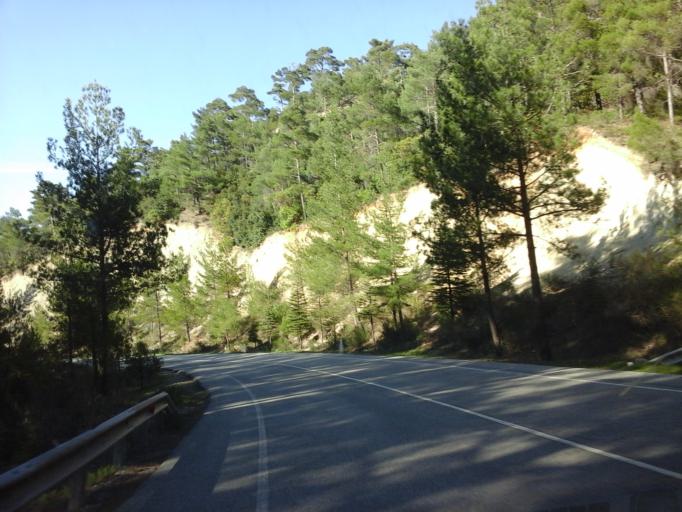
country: CY
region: Lefkosia
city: Kakopetria
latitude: 34.9535
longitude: 32.9284
